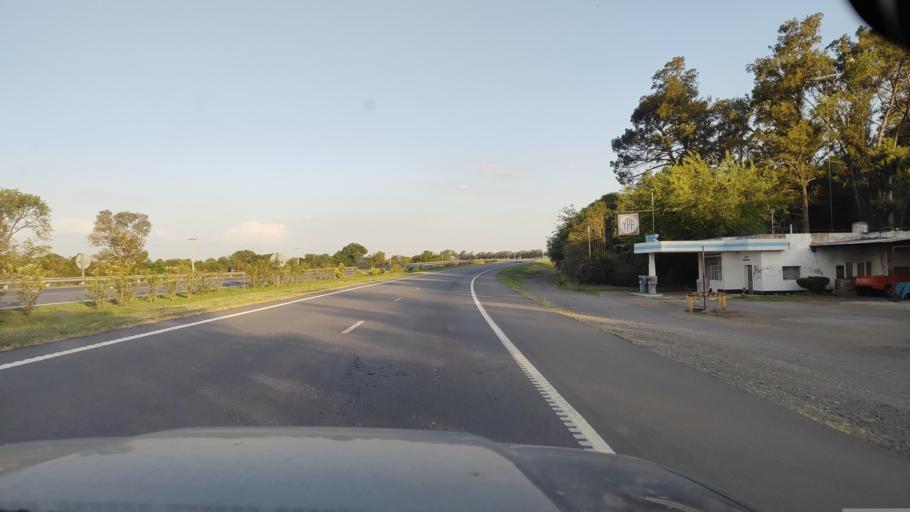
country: AR
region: Buenos Aires
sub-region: Partido de Lujan
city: Lujan
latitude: -34.5474
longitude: -59.2012
